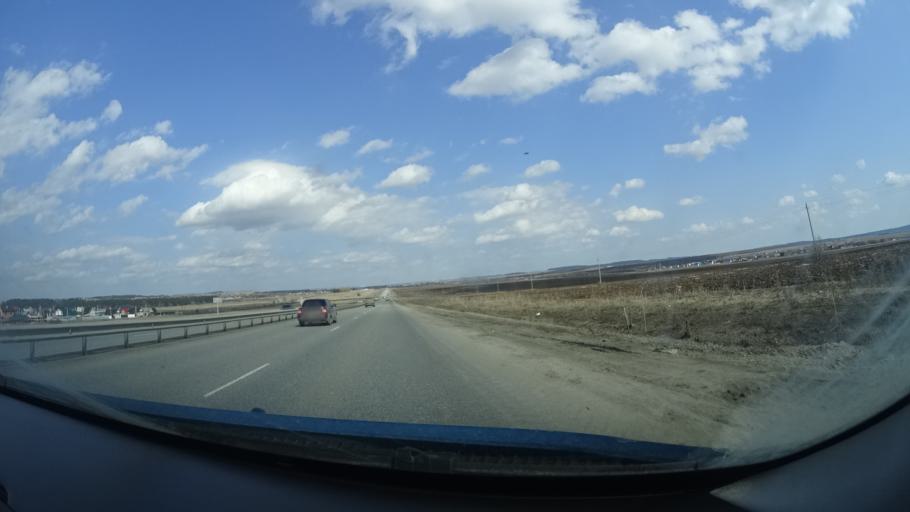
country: RU
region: Perm
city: Kultayevo
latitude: 57.8719
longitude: 55.8959
